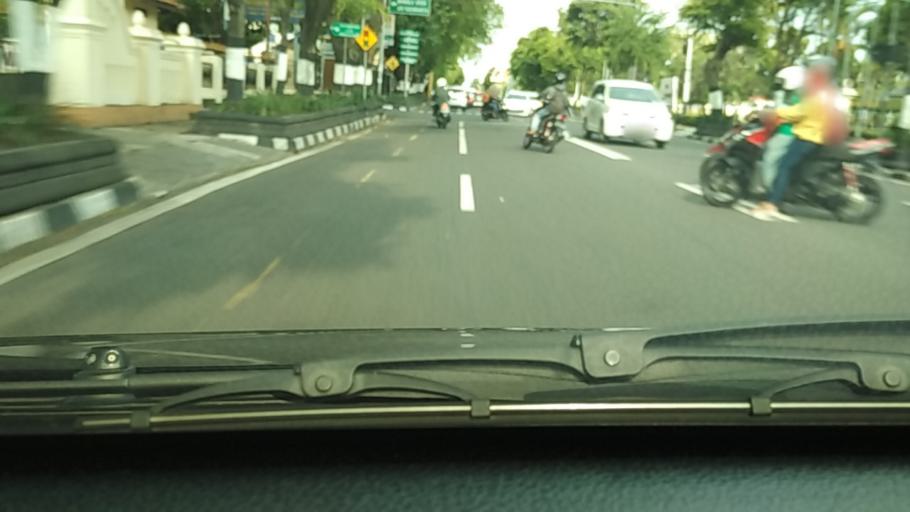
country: ID
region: Daerah Istimewa Yogyakarta
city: Yogyakarta
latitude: -7.8018
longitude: 110.3826
